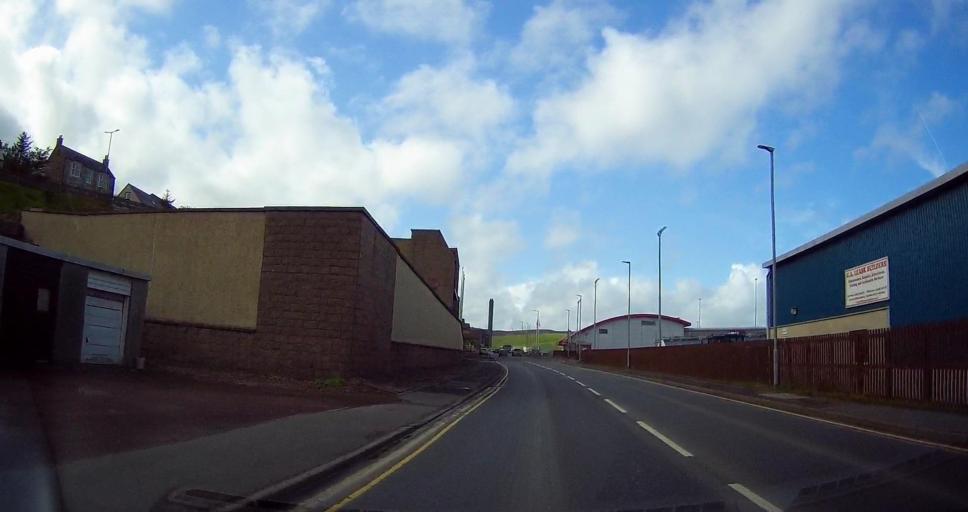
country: GB
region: Scotland
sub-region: Shetland Islands
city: Lerwick
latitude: 60.1609
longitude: -1.1578
